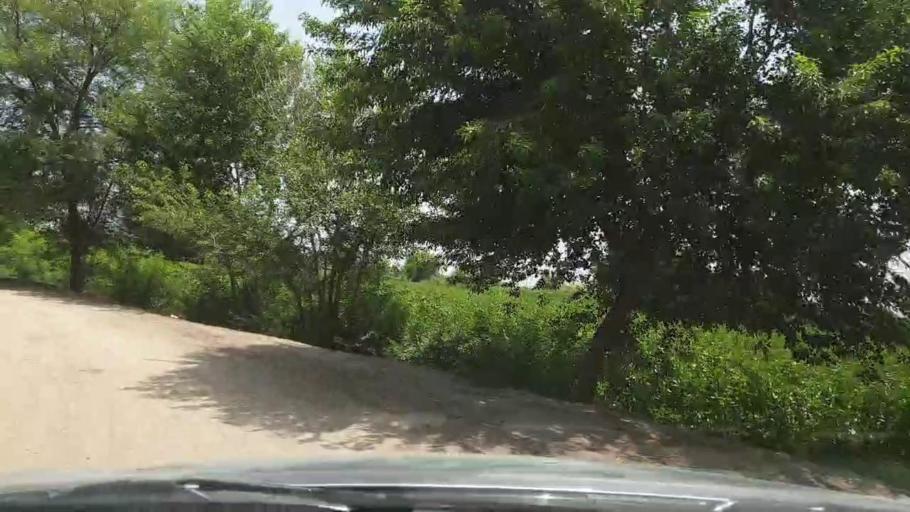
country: PK
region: Sindh
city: Pano Aqil
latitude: 27.8681
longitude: 69.1760
